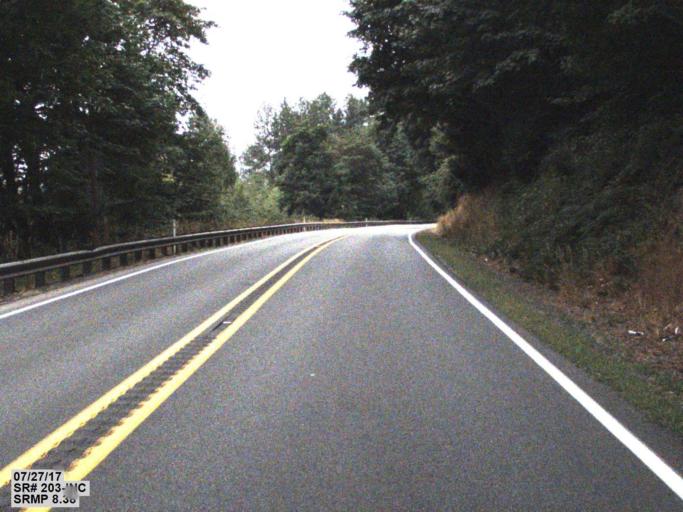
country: US
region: Washington
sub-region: King County
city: Lake Marcel-Stillwater
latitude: 47.6798
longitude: -121.9118
